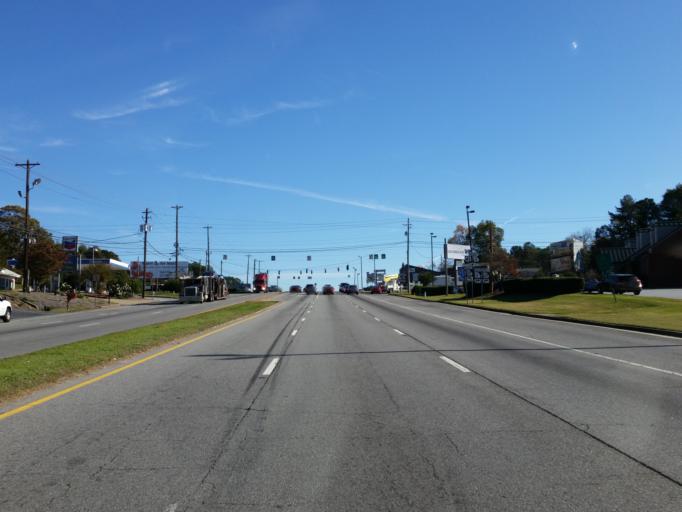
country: US
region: Georgia
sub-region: Cobb County
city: Marietta
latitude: 33.9615
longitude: -84.5294
